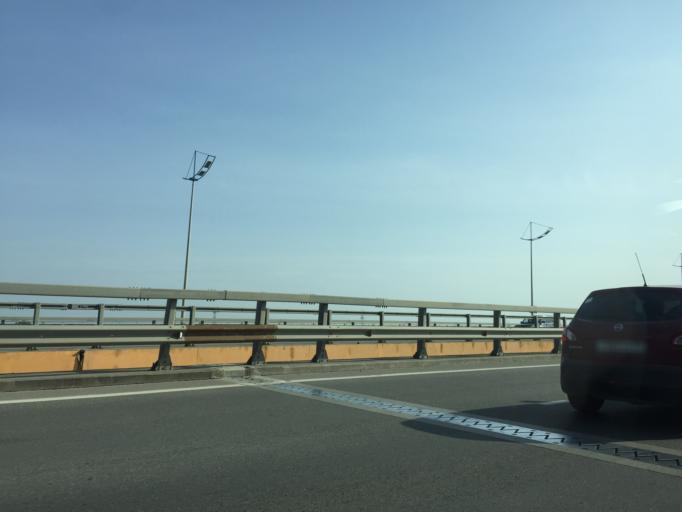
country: RU
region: Kaliningrad
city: Bol'shoe Isakovo
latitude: 54.6943
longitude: 20.5983
